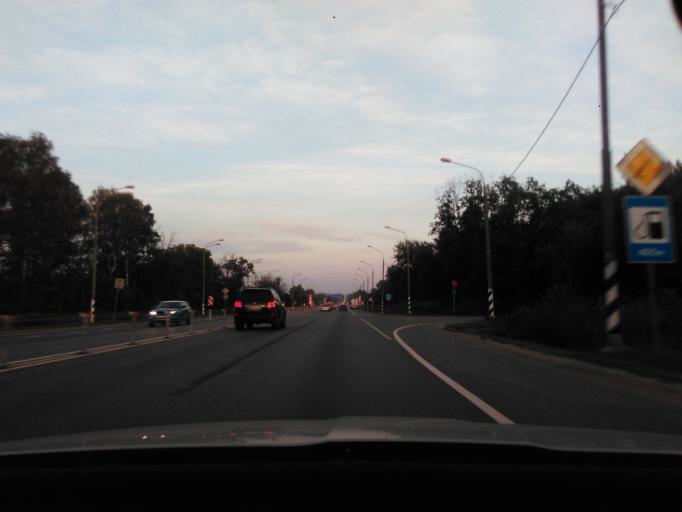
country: RU
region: Moskovskaya
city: Klin
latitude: 56.3111
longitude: 36.7775
